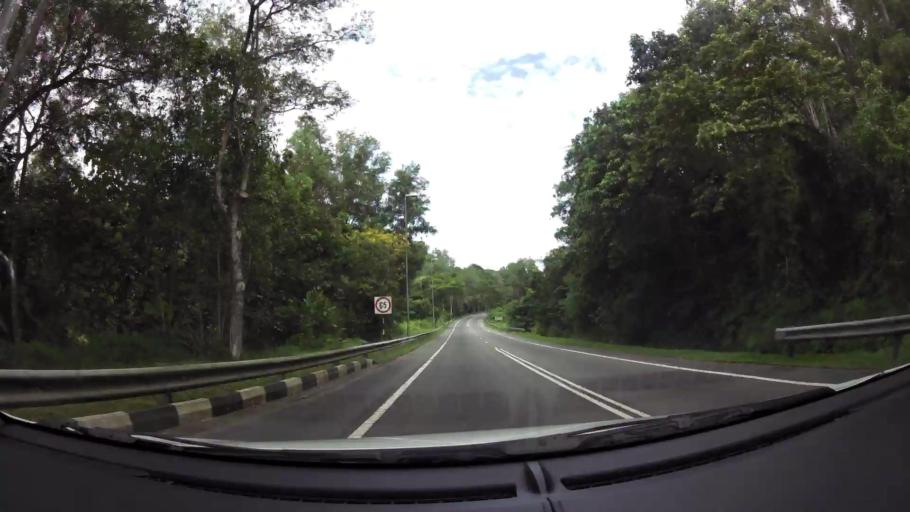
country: BN
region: Brunei and Muara
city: Bandar Seri Begawan
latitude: 4.8772
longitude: 114.8973
